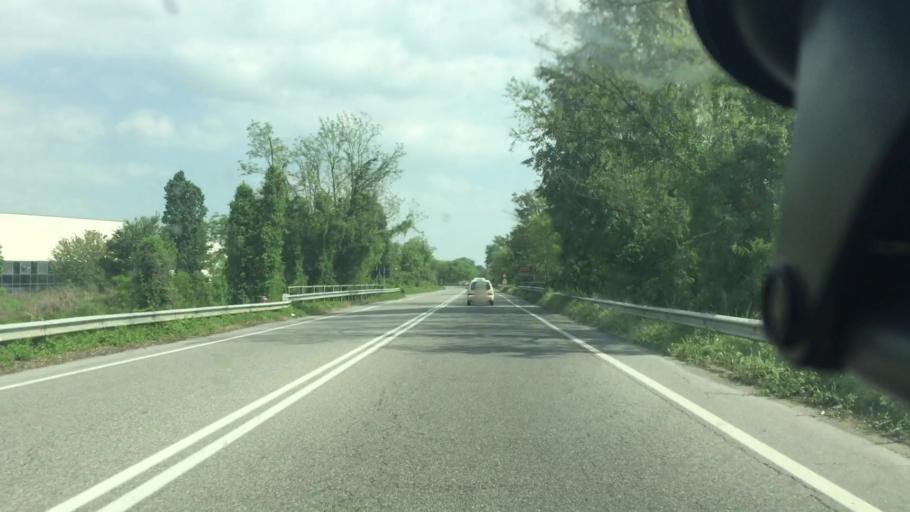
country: IT
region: Lombardy
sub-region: Citta metropolitana di Milano
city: Sant'Agata Martesana
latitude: 45.5232
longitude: 9.3943
